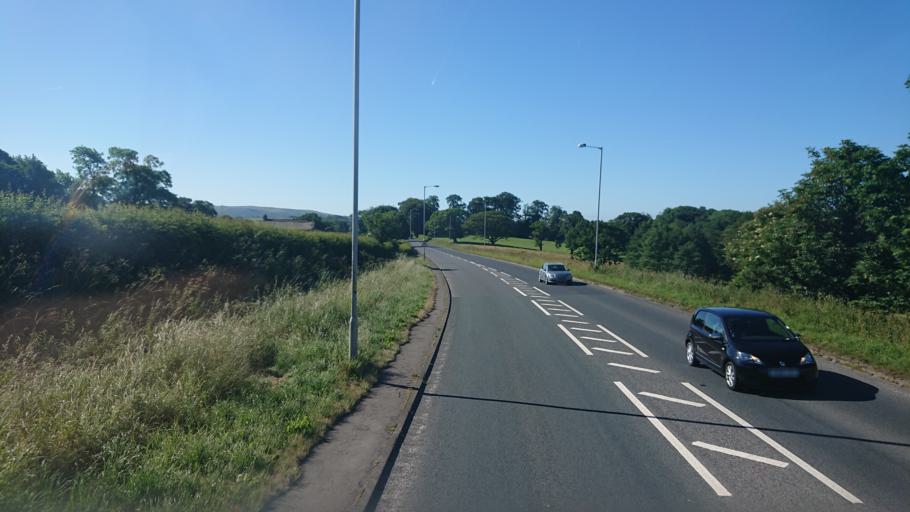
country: GB
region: England
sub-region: Lancashire
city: Galgate
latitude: 53.9746
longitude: -2.7847
